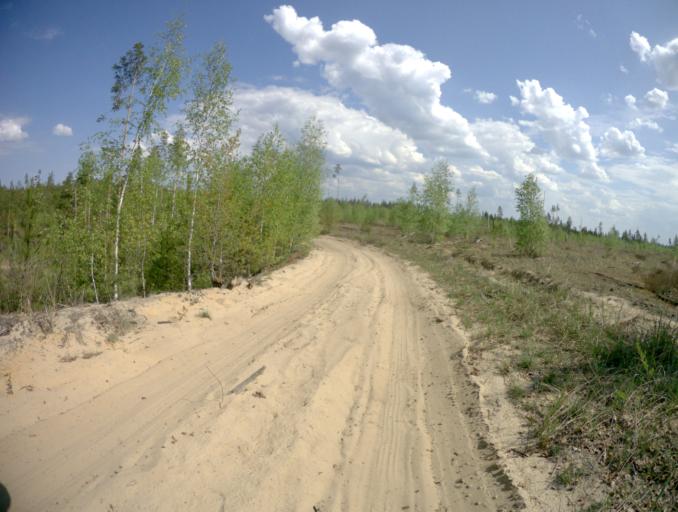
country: RU
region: Ivanovo
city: Talitsy
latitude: 56.4671
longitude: 42.1835
